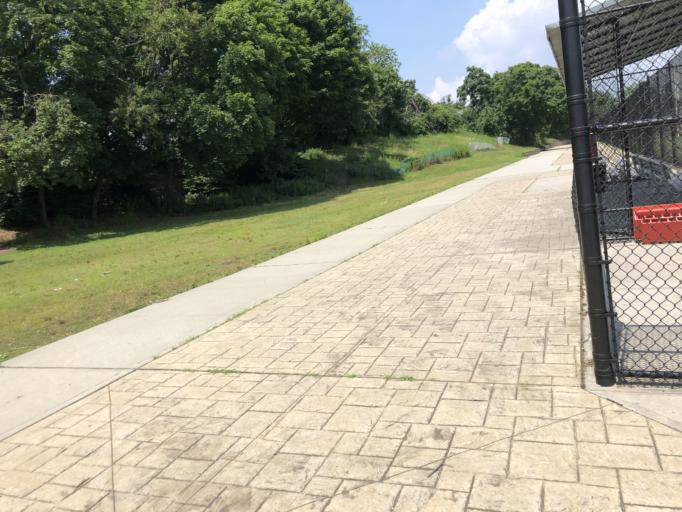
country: US
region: New York
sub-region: Nassau County
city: Hewlett
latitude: 40.6441
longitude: -73.6897
